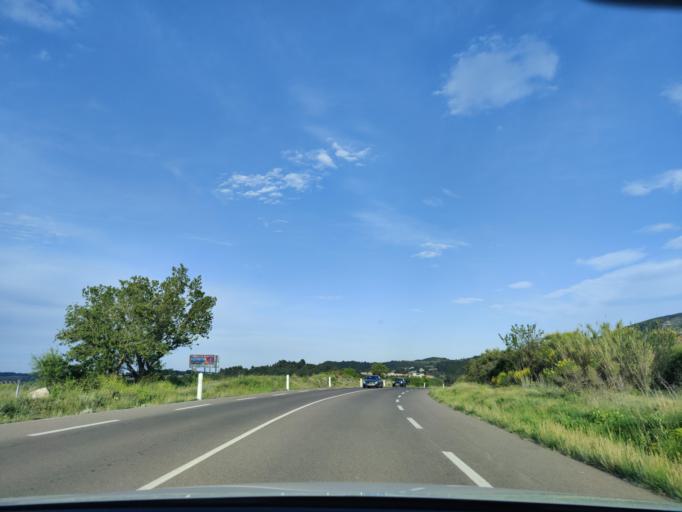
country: FR
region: Languedoc-Roussillon
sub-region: Departement des Pyrenees-Orientales
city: Baixas
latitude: 42.7780
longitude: 2.7724
